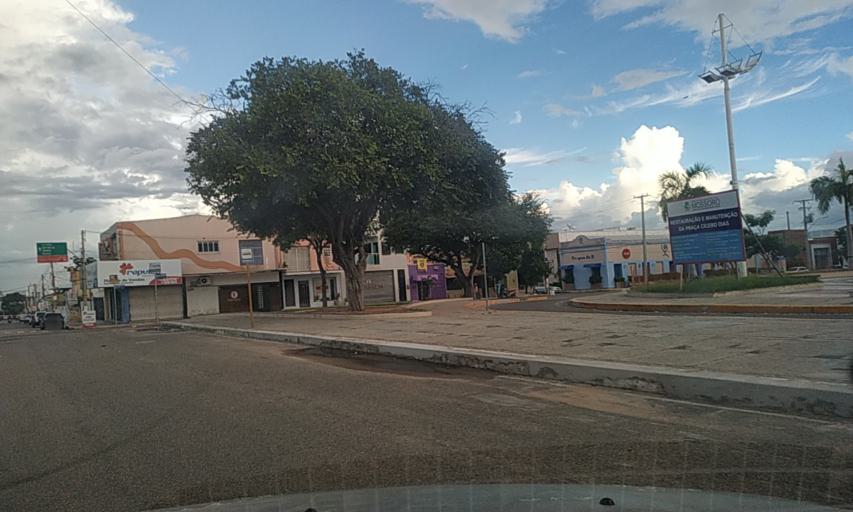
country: BR
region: Rio Grande do Norte
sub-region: Mossoro
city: Mossoro
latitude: -5.1901
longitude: -37.3455
